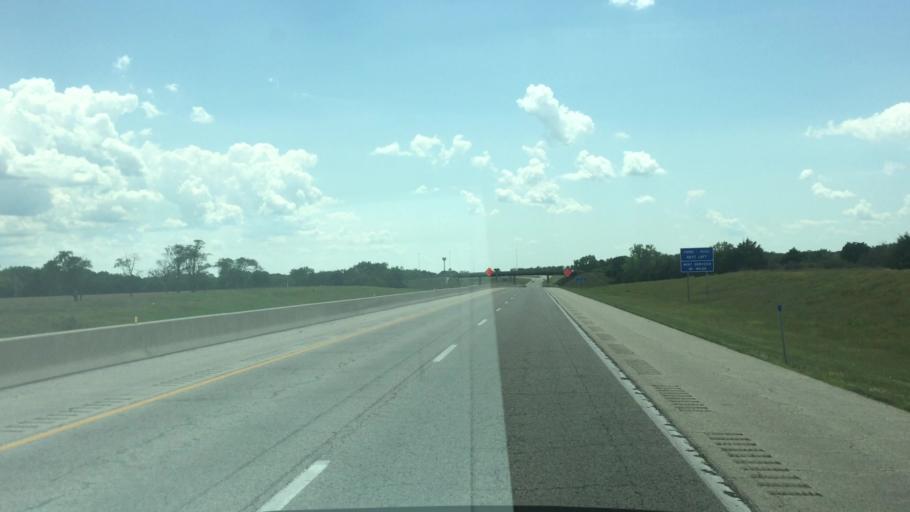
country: US
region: Kansas
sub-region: Lyon County
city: Emporia
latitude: 38.4805
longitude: -96.1760
